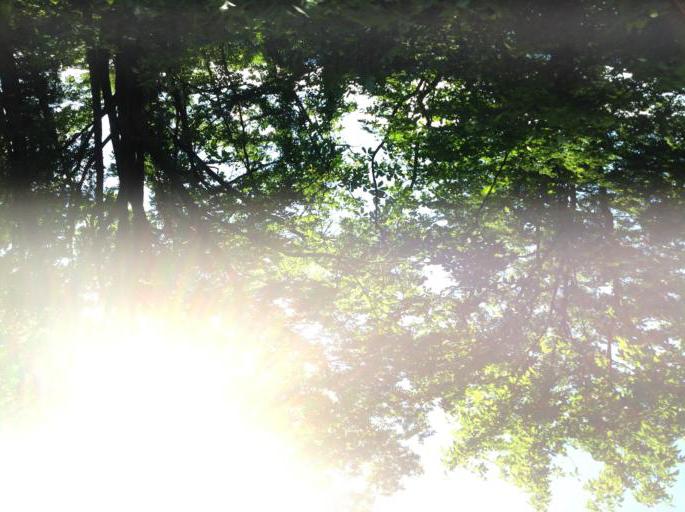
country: JP
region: Akita
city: Kakunodatemachi
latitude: 39.7016
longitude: 140.6453
